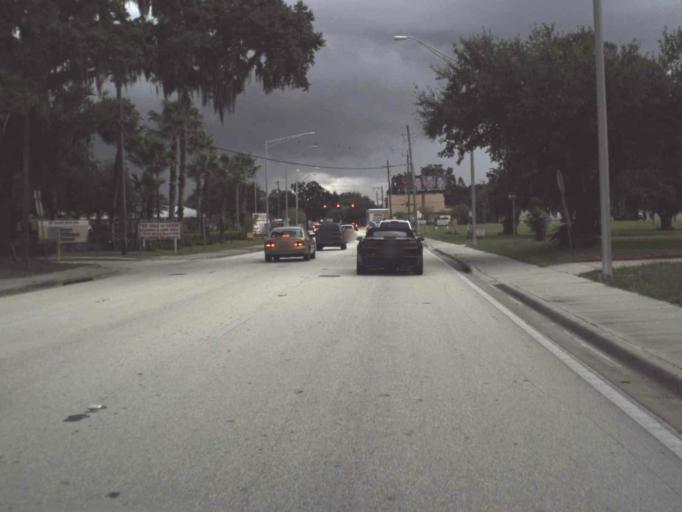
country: US
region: Florida
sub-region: Manatee County
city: Bradenton
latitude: 27.4939
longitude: -82.5572
